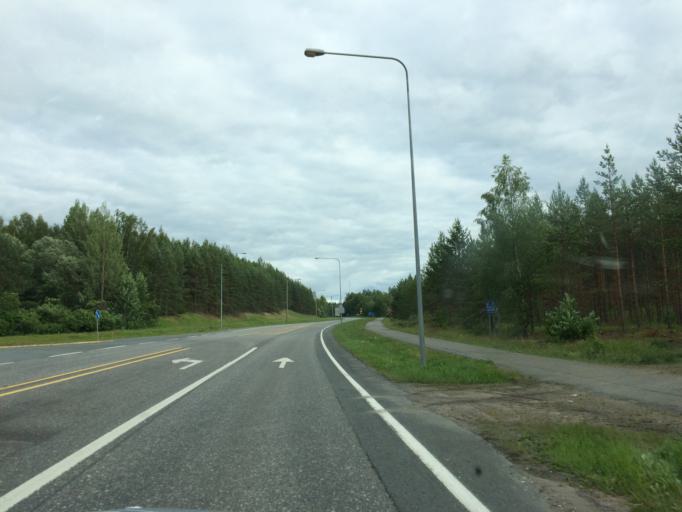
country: FI
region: Haeme
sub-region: Haemeenlinna
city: Haemeenlinna
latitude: 60.9717
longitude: 24.4767
